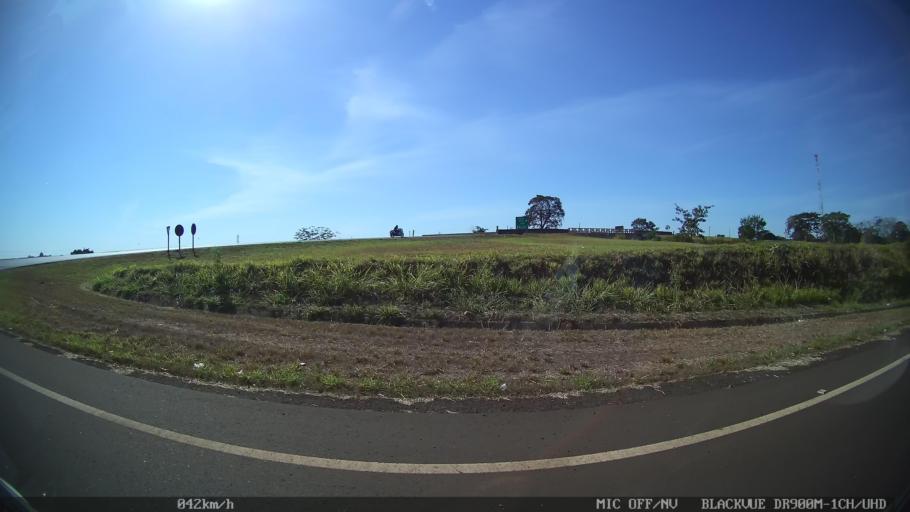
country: BR
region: Sao Paulo
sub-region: Olimpia
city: Olimpia
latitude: -20.6856
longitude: -48.9049
